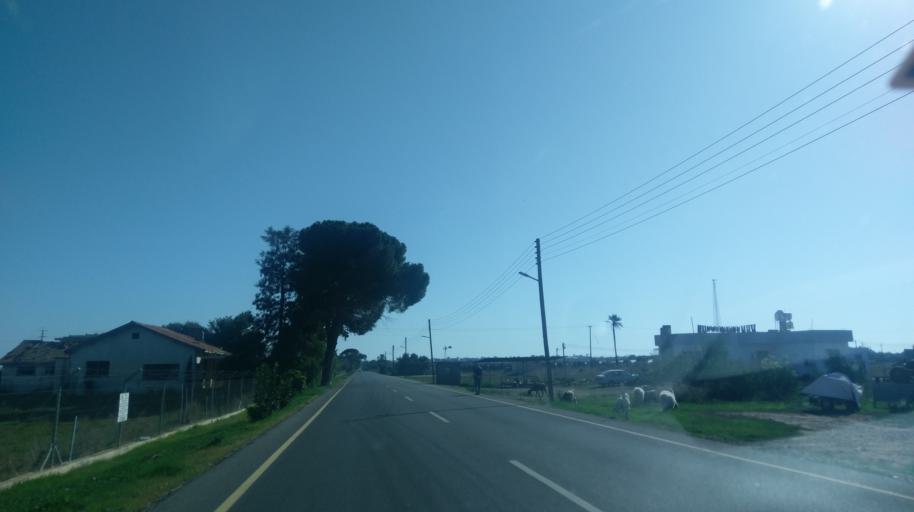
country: CY
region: Ammochostos
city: Deryneia
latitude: 35.0931
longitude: 33.9523
